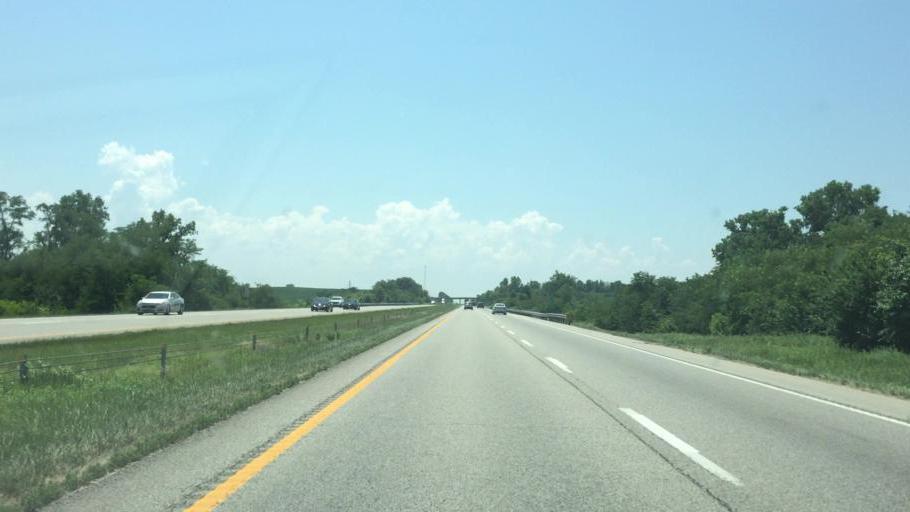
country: US
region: Missouri
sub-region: Platte County
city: Weston
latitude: 39.5648
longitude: -94.7884
